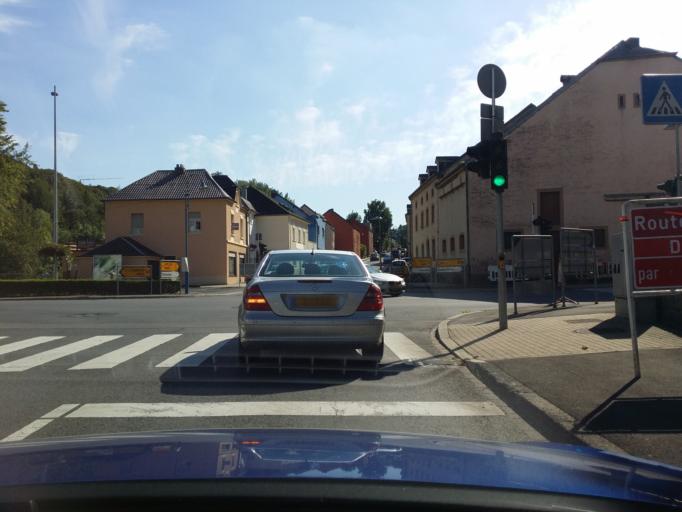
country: LU
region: Luxembourg
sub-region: Canton de Capellen
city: Kopstal
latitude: 49.6646
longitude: 6.0722
